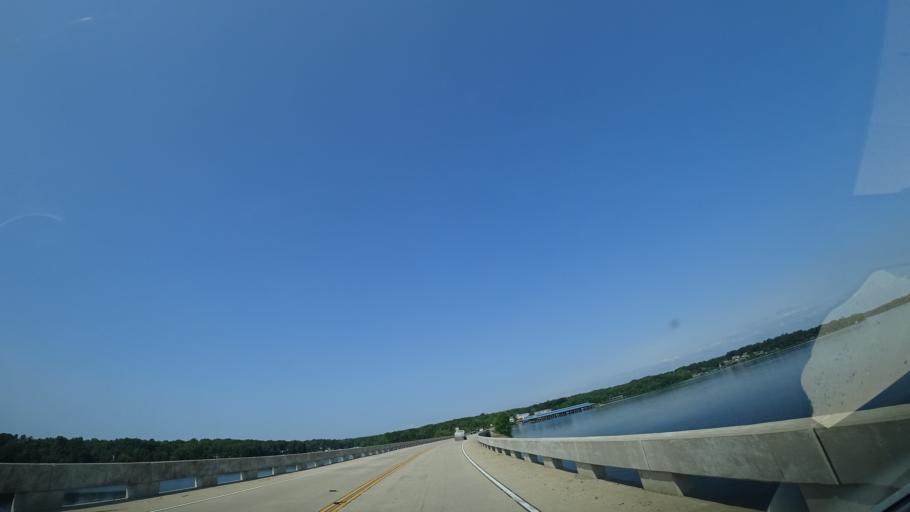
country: US
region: Virginia
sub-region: Louisa County
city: Louisa
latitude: 38.0851
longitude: -77.8137
